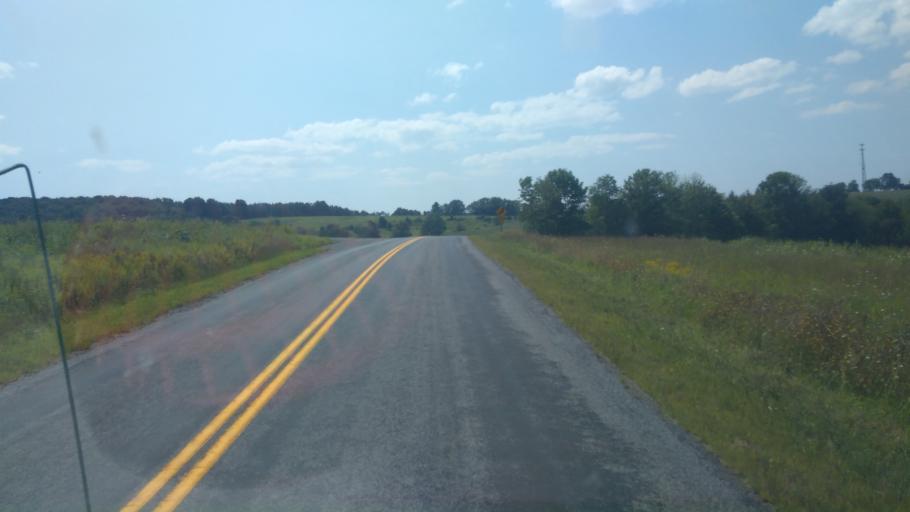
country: US
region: New York
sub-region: Steuben County
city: Canisteo
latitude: 42.3511
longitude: -77.5687
